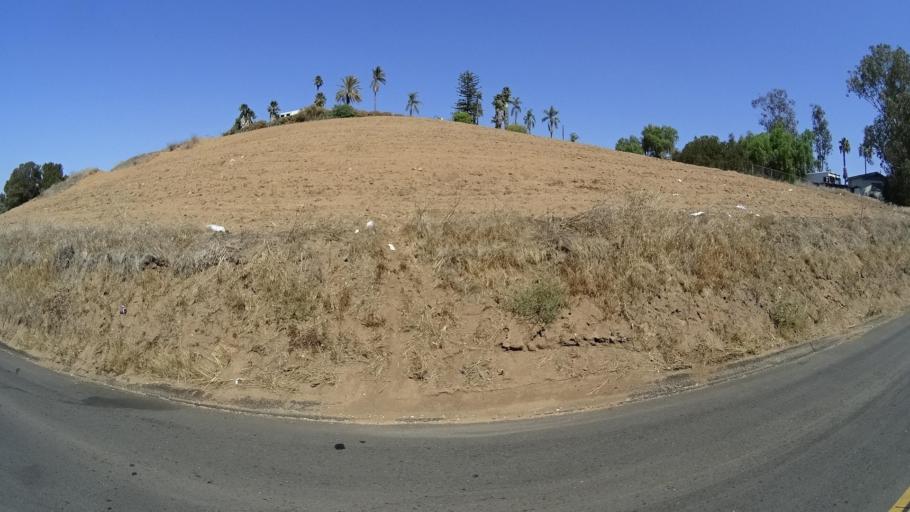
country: US
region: California
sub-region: San Diego County
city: Lake San Marcos
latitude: 33.1692
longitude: -117.2089
